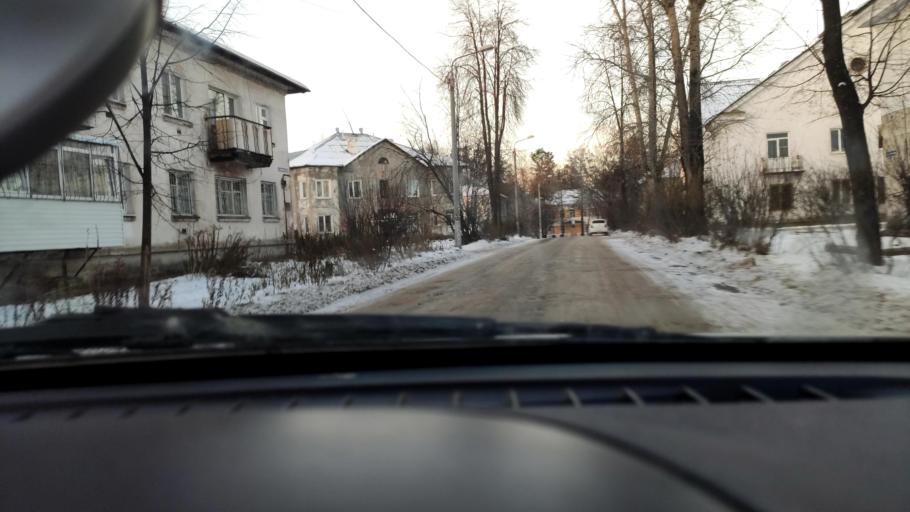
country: RU
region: Perm
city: Perm
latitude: 58.1126
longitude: 56.3161
